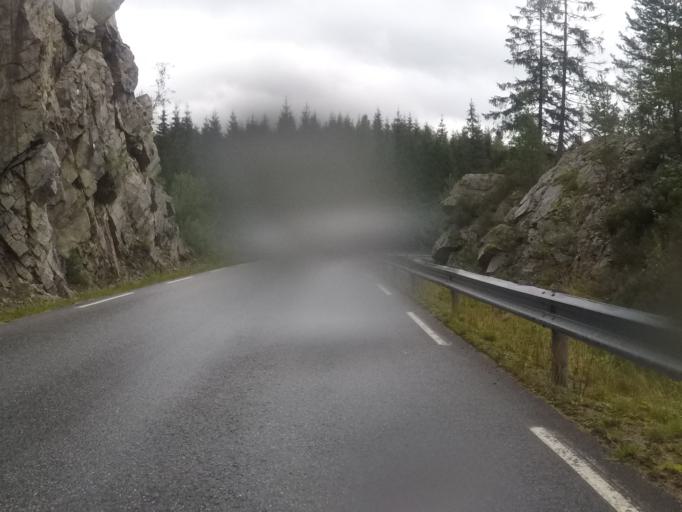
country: NO
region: Vest-Agder
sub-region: Audnedal
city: Konsmo
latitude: 58.2808
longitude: 7.3455
